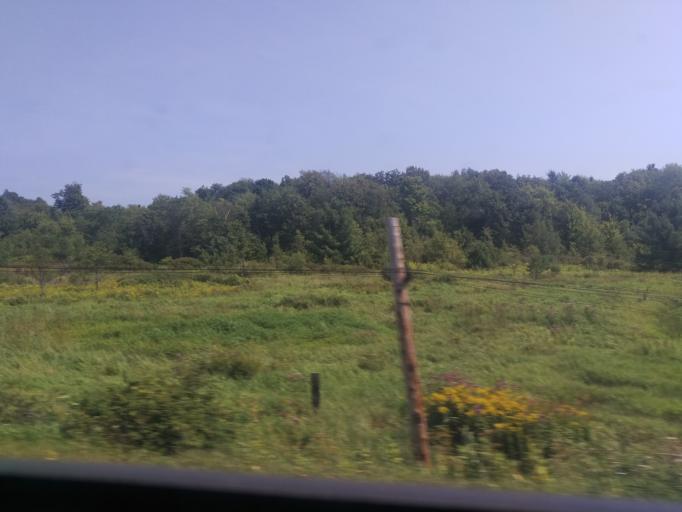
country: US
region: New York
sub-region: Jefferson County
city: Alexandria Bay
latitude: 44.4478
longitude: -75.9403
